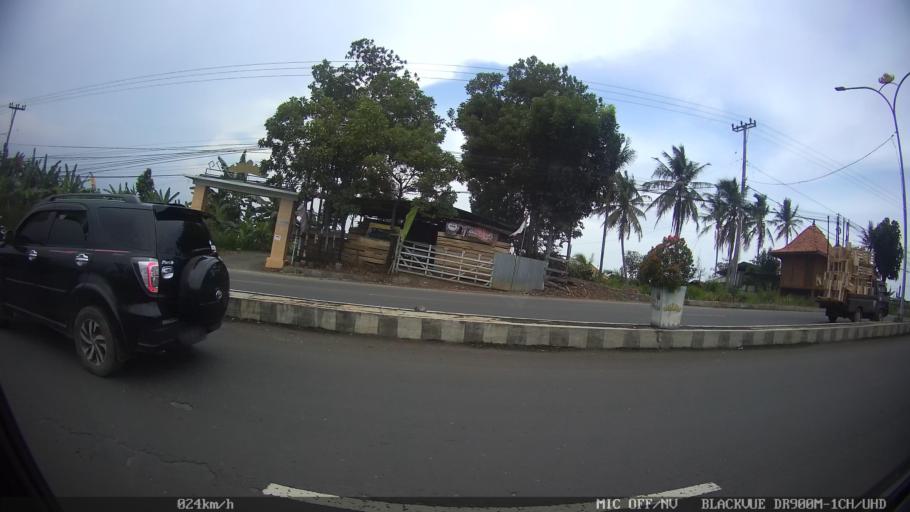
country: ID
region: Lampung
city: Kedaton
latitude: -5.3896
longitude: 105.2199
